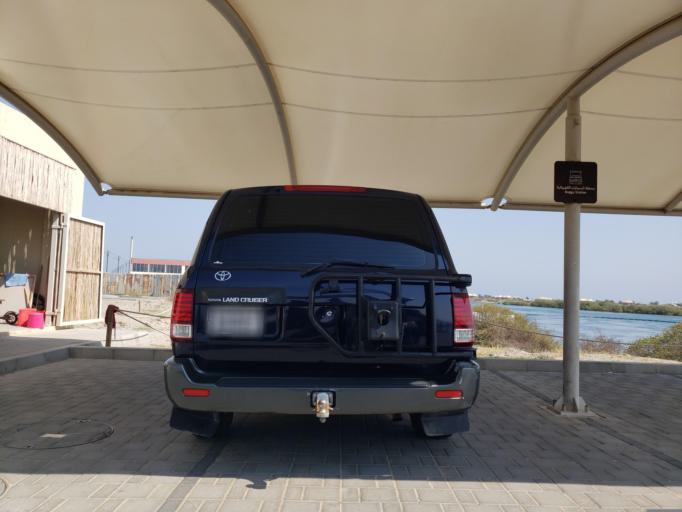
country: AE
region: Al Fujayrah
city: Al Fujayrah
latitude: 25.0150
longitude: 56.3605
